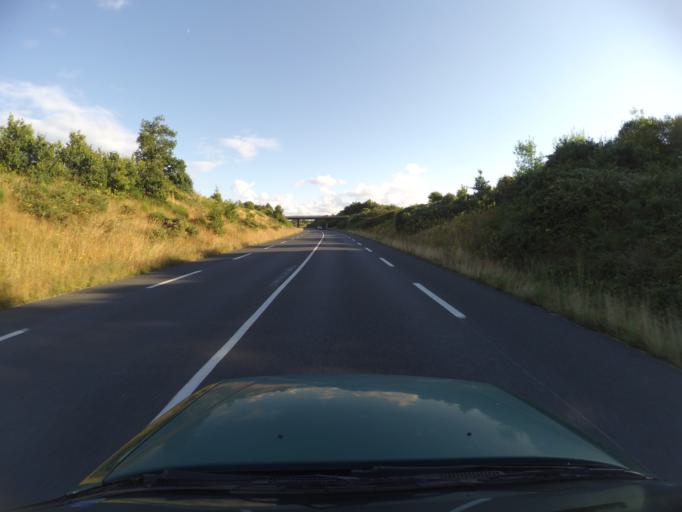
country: FR
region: Pays de la Loire
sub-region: Departement de la Vendee
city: Bouffere
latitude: 46.9859
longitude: -1.3541
